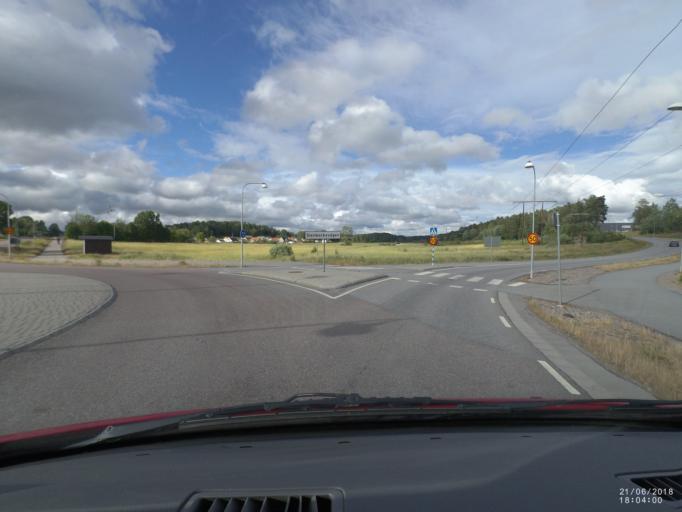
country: SE
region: Soedermanland
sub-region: Nykopings Kommun
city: Nykoping
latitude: 58.7708
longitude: 17.0071
